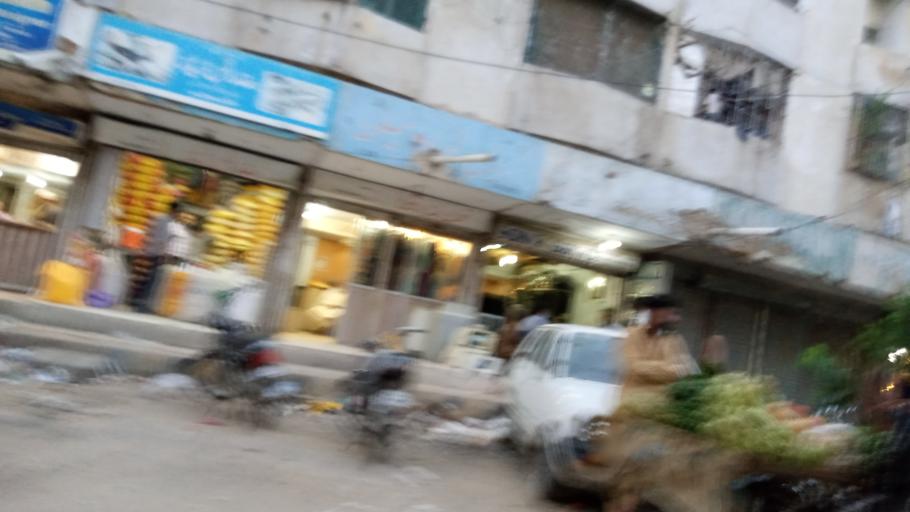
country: PK
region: Sindh
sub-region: Karachi District
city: Karachi
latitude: 24.9390
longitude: 67.0808
